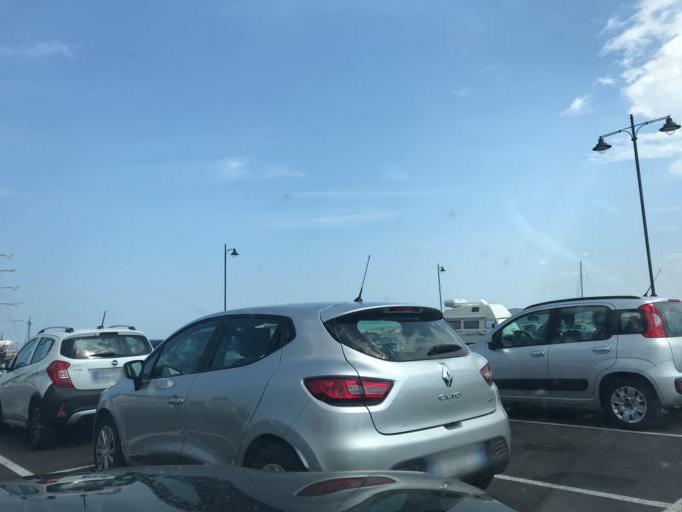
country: IT
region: Sardinia
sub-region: Provincia di Olbia-Tempio
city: Olbia
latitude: 40.9221
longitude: 9.5054
